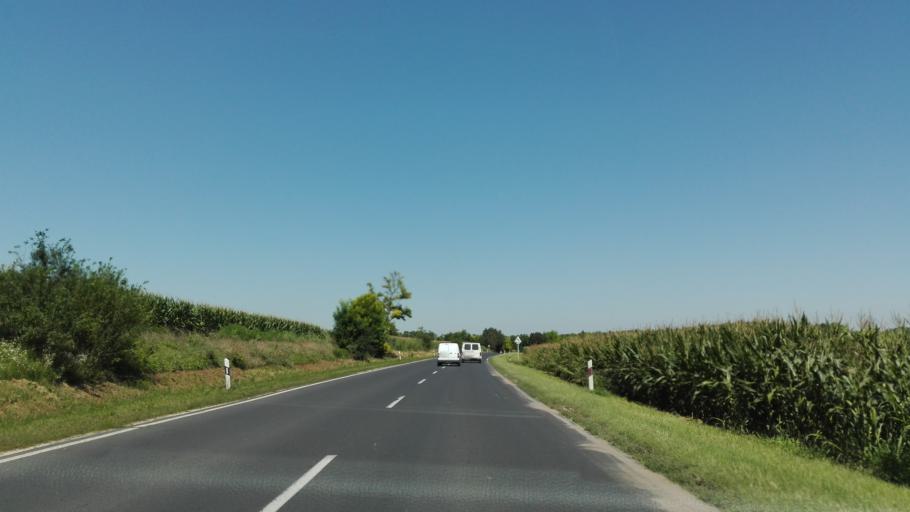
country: HU
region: Fejer
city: Mezoszilas
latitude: 46.7974
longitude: 18.4916
